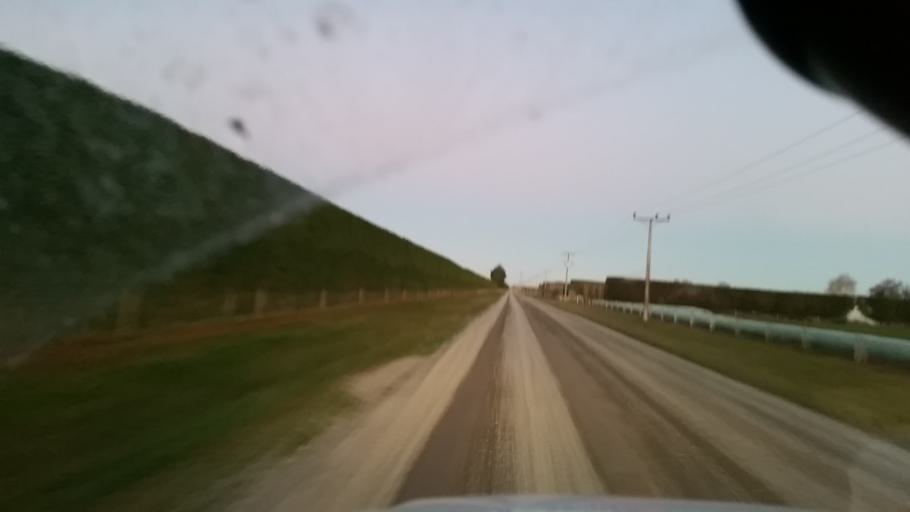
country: NZ
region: Canterbury
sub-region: Ashburton District
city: Tinwald
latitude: -43.9721
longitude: 171.6383
